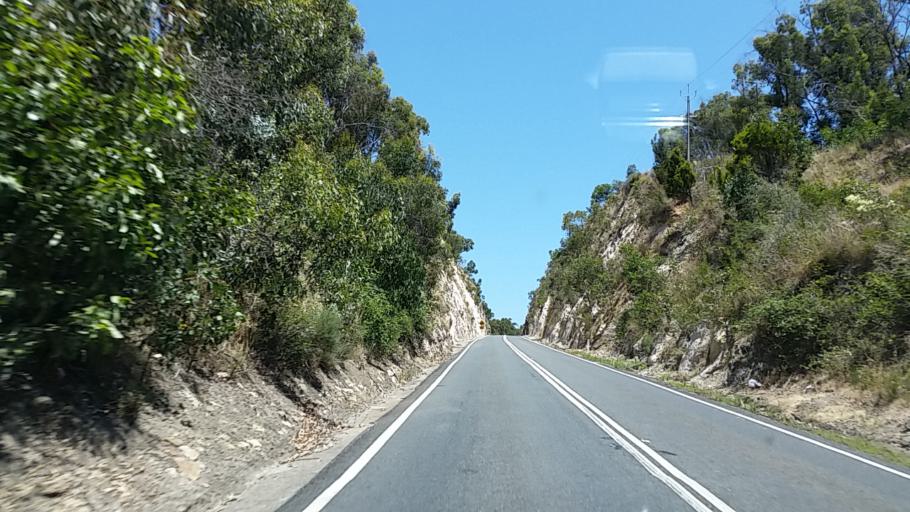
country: AU
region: South Australia
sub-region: Tea Tree Gully
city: Golden Grove
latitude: -34.8191
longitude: 138.7946
